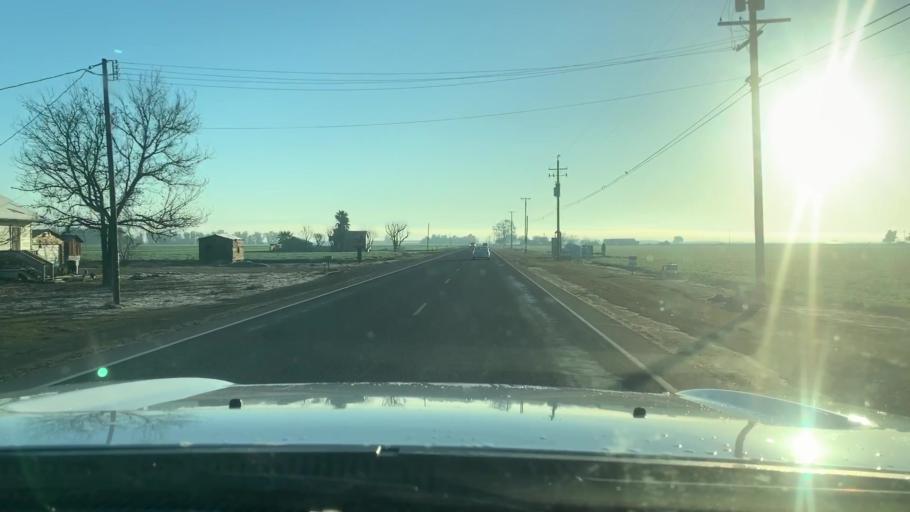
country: US
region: California
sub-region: Kings County
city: Home Garden
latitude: 36.2113
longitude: -119.6343
